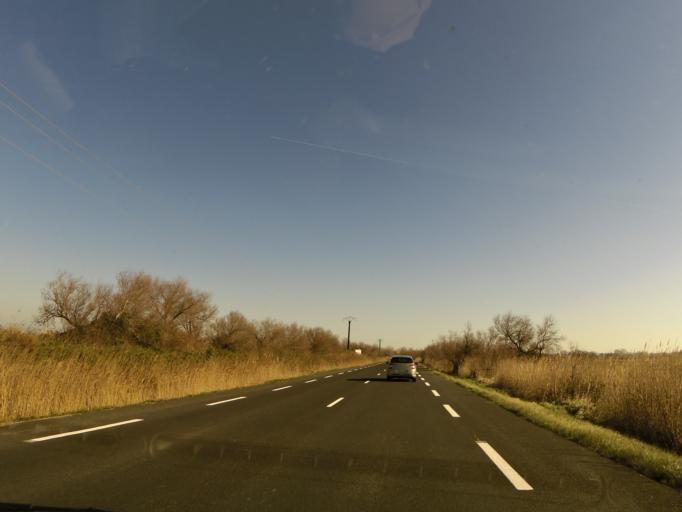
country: FR
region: Provence-Alpes-Cote d'Azur
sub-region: Departement des Bouches-du-Rhone
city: Saintes-Maries-de-la-Mer
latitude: 43.5501
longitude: 4.3392
